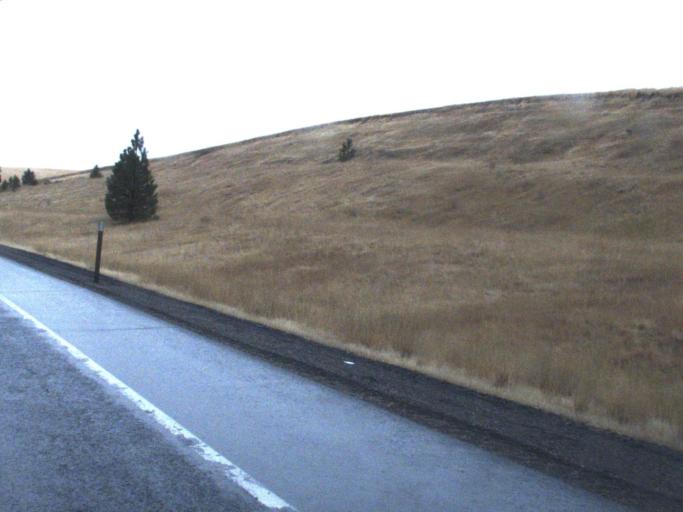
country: US
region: Washington
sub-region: Whitman County
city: Colfax
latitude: 47.2234
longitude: -117.3534
